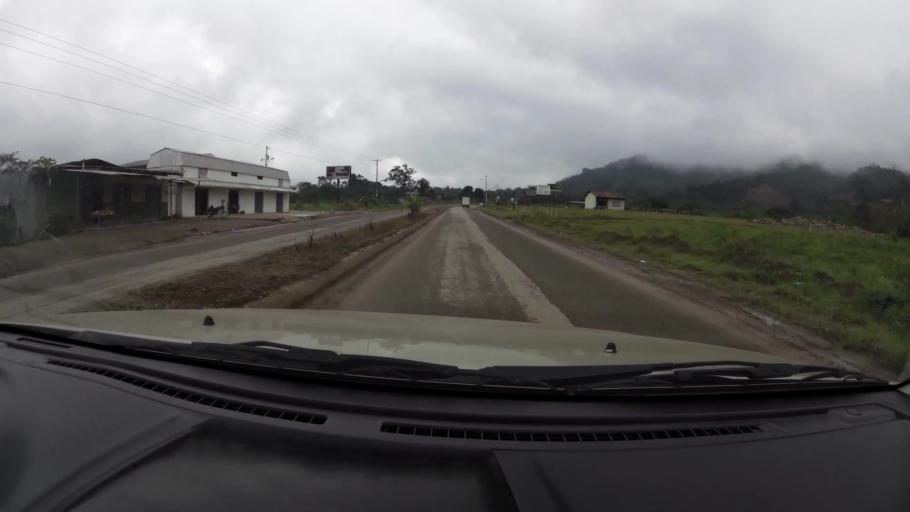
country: EC
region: El Oro
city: Pasaje
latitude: -3.3283
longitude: -79.7738
